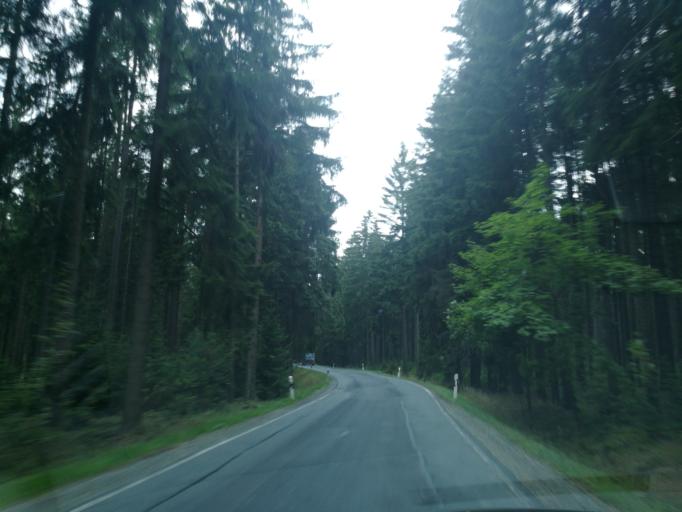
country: DE
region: Saxony
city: Eichigt
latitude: 50.3323
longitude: 12.1419
